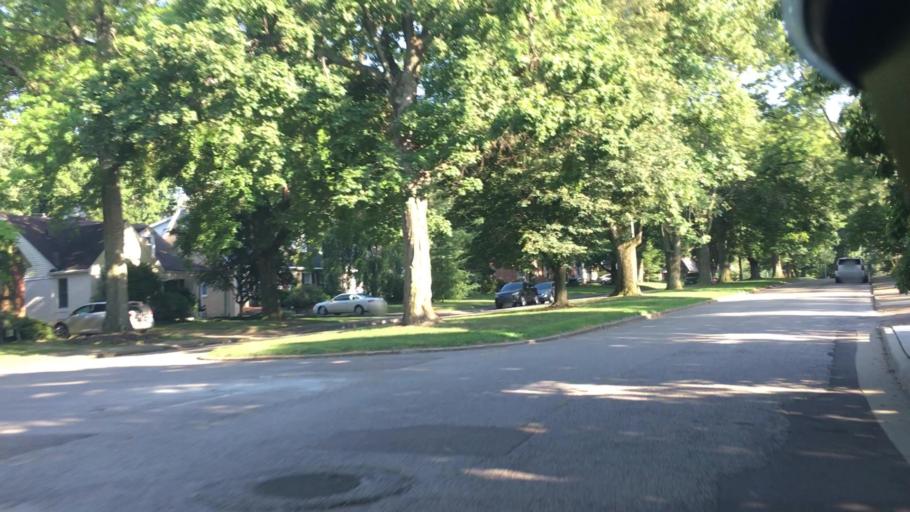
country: US
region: Indiana
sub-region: Vanderburgh County
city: Evansville
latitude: 37.9728
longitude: -87.5246
